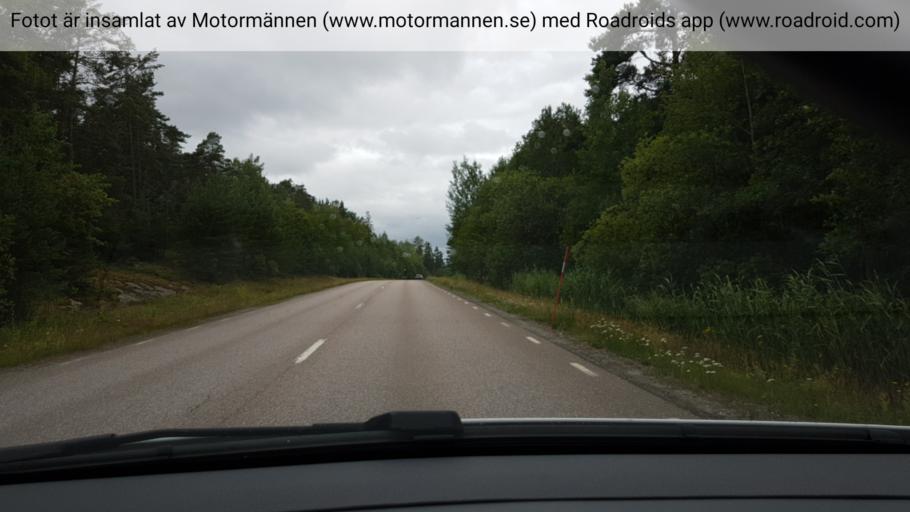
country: SE
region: Stockholm
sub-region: Vaxholms Kommun
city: Vaxholm
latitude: 59.3947
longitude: 18.4200
